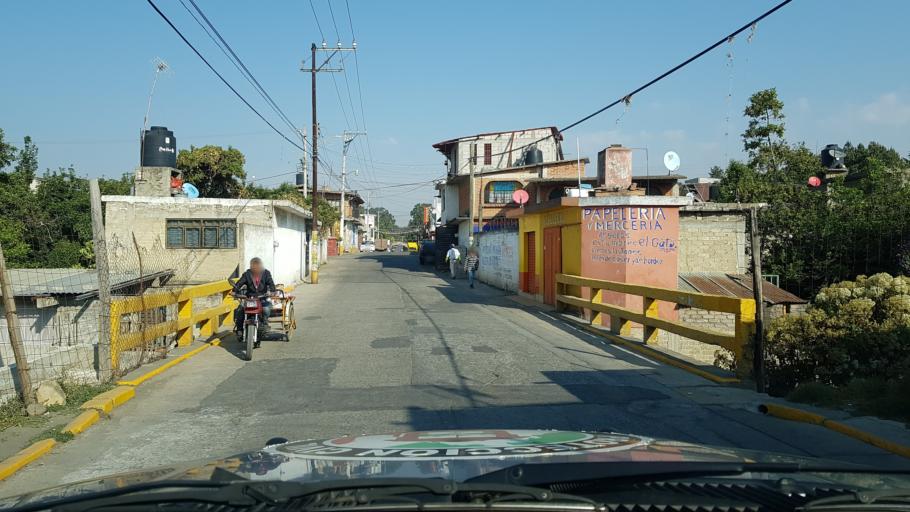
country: MX
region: Mexico
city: Ozumba de Alzate
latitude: 19.0561
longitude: -98.7731
